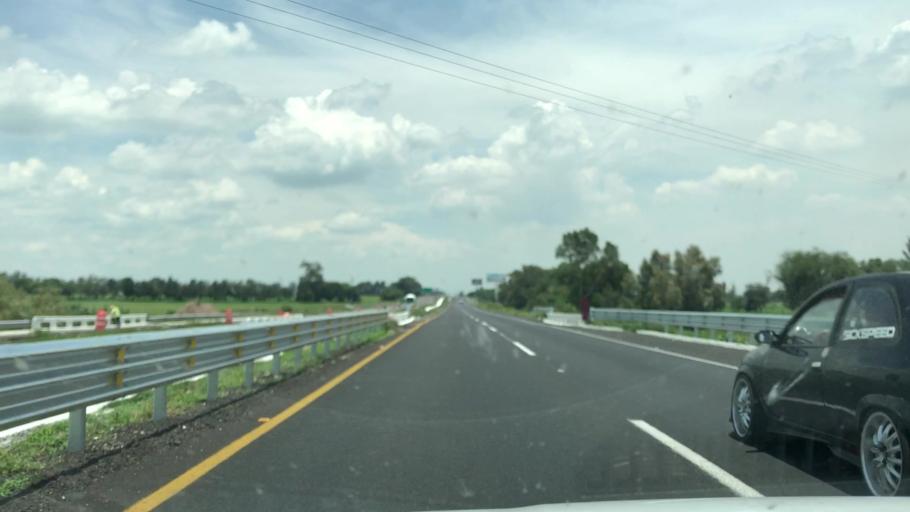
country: MX
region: Guanajuato
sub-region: Irapuato
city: Cuarta Brigada
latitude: 20.6529
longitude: -101.2870
